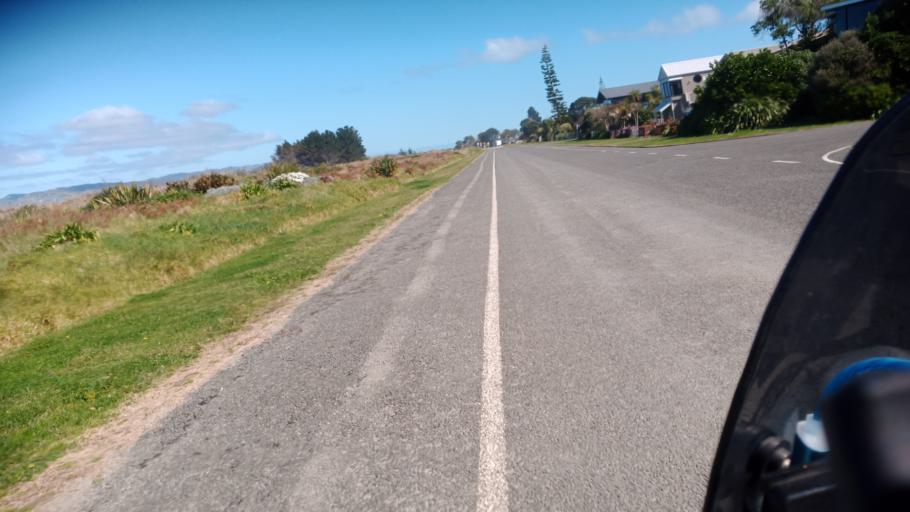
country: NZ
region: Gisborne
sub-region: Gisborne District
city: Gisborne
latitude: -39.0154
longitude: 177.8858
